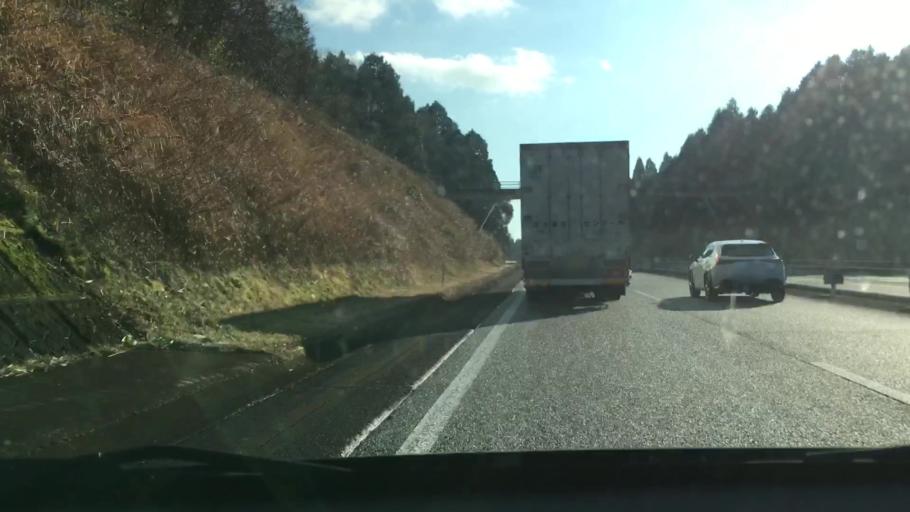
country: JP
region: Kagoshima
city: Okuchi-shinohara
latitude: 31.9293
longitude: 130.7048
